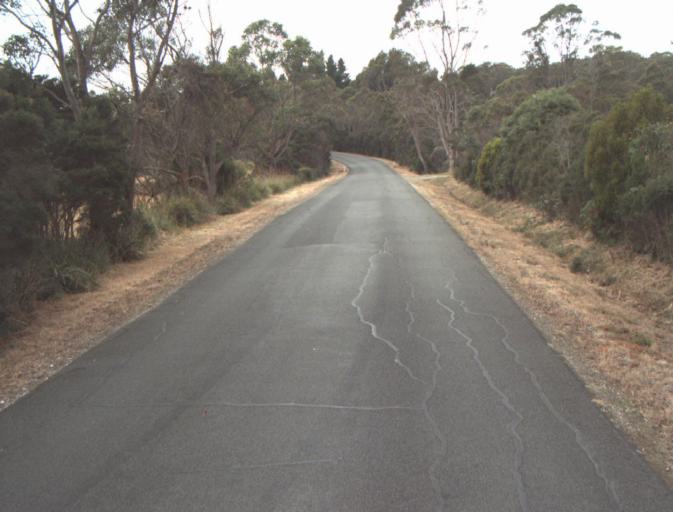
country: AU
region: Tasmania
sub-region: Launceston
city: Mayfield
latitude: -41.2234
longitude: 147.0432
